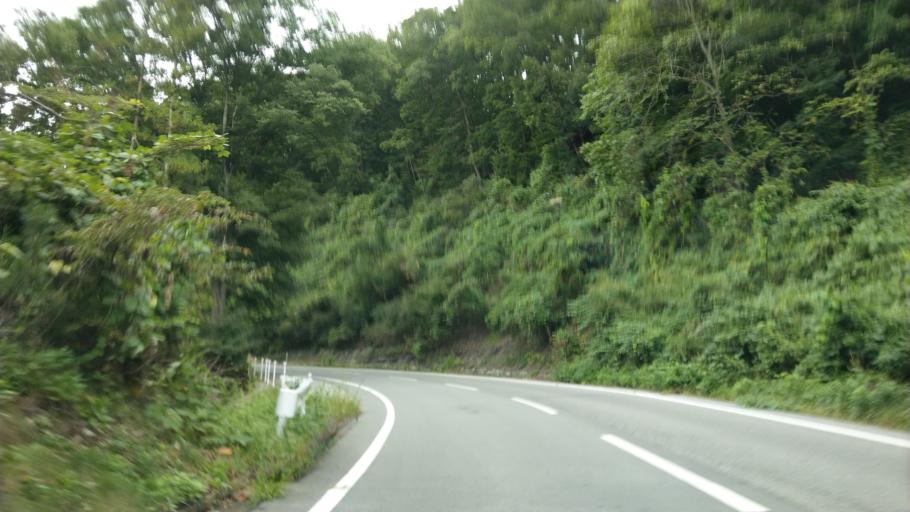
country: JP
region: Nagano
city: Komoro
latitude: 36.3224
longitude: 138.3911
